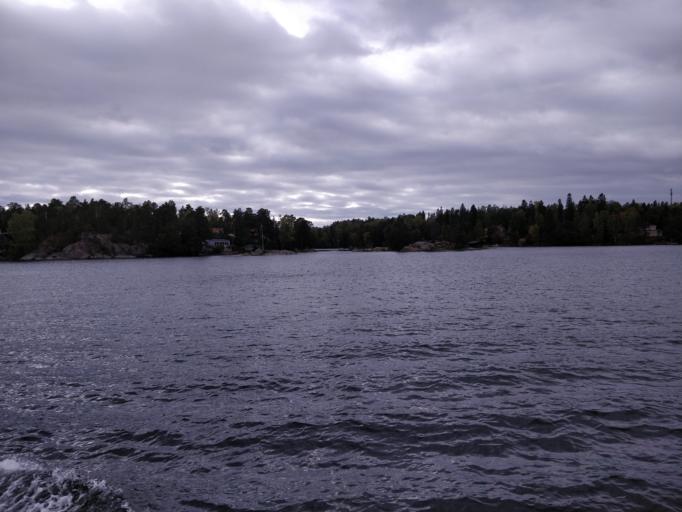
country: FI
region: Uusimaa
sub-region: Helsinki
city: Vantaa
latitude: 60.1711
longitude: 25.0931
